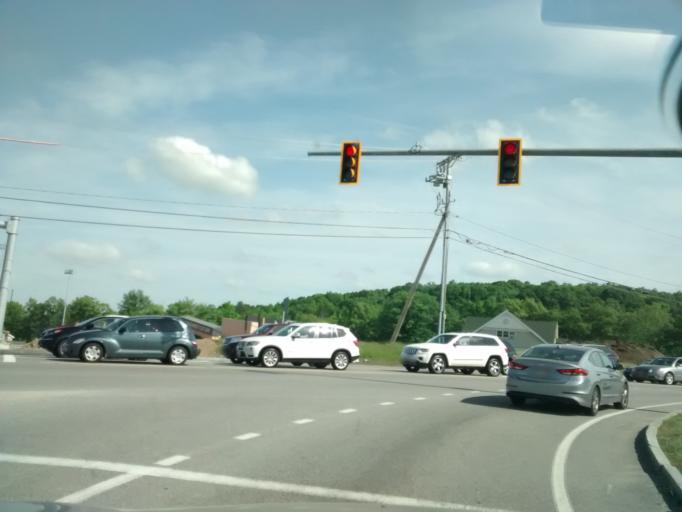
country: US
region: Massachusetts
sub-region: Worcester County
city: Northborough
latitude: 42.2858
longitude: -71.6685
